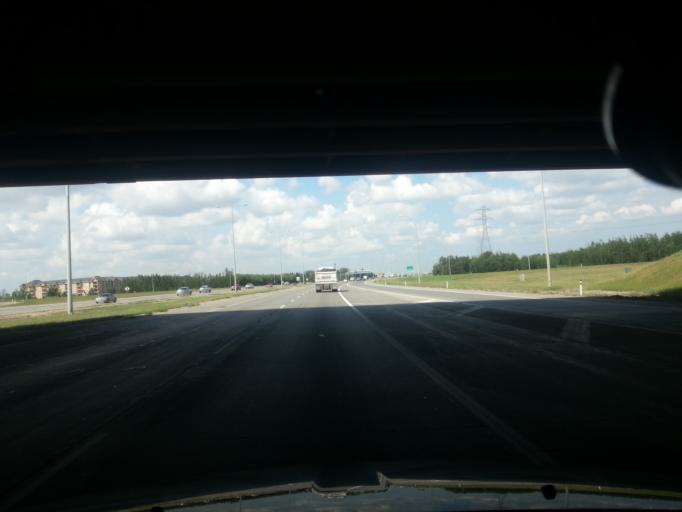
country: CA
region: Alberta
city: Devon
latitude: 53.4800
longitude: -113.6581
